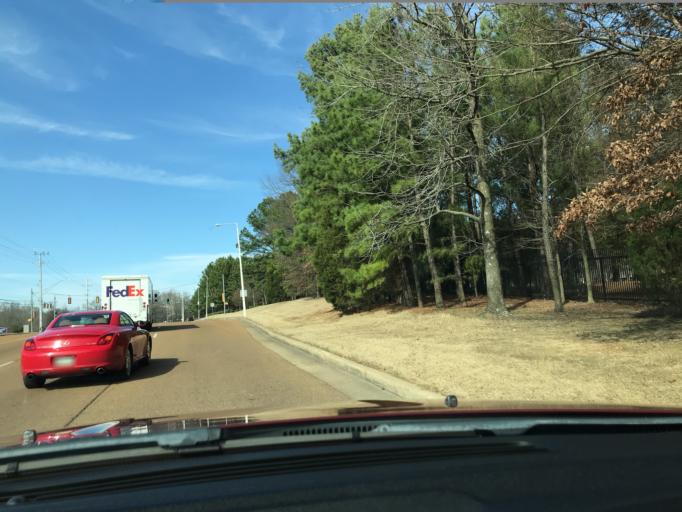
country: US
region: Tennessee
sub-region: Shelby County
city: Germantown
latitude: 35.0497
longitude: -89.7951
